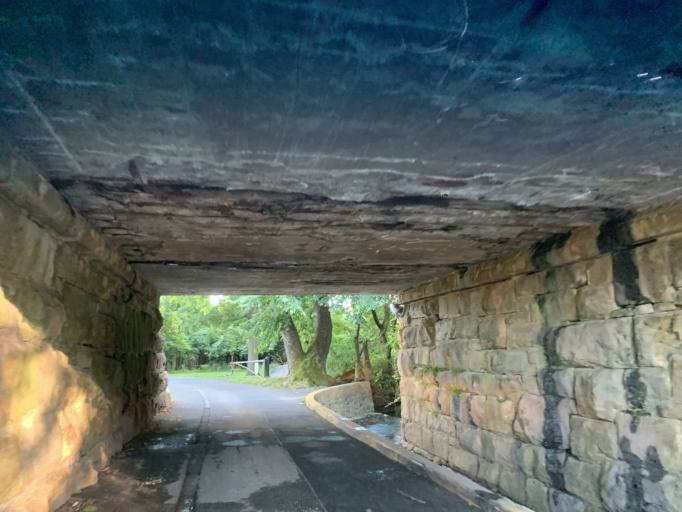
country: US
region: Maryland
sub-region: Harford County
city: Havre de Grace
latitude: 39.5316
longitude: -76.1273
